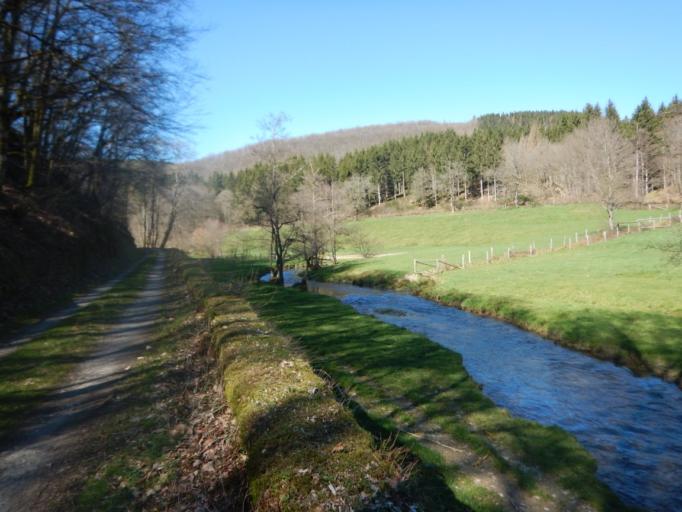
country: LU
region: Diekirch
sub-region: Canton de Wiltz
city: Wilwerwiltz
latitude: 49.9707
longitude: 5.9734
